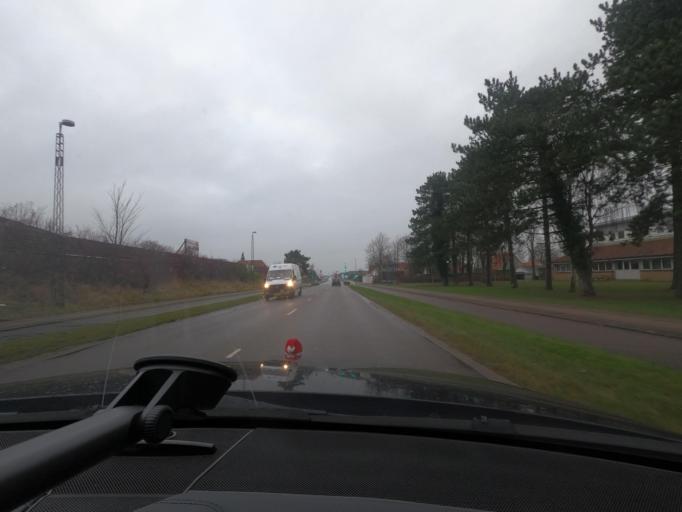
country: DK
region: South Denmark
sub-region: Sonderborg Kommune
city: Sonderborg
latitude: 54.9144
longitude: 9.8107
